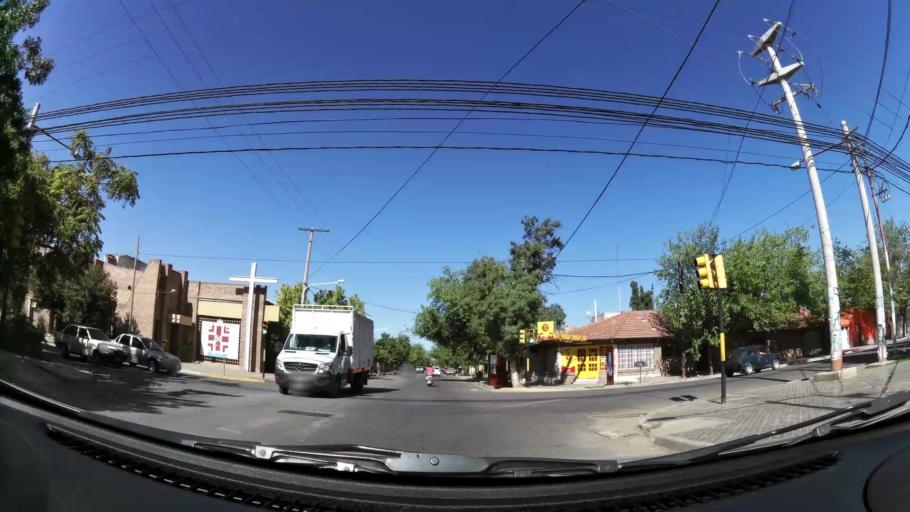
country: AR
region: Mendoza
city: Mendoza
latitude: -32.8932
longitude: -68.8083
